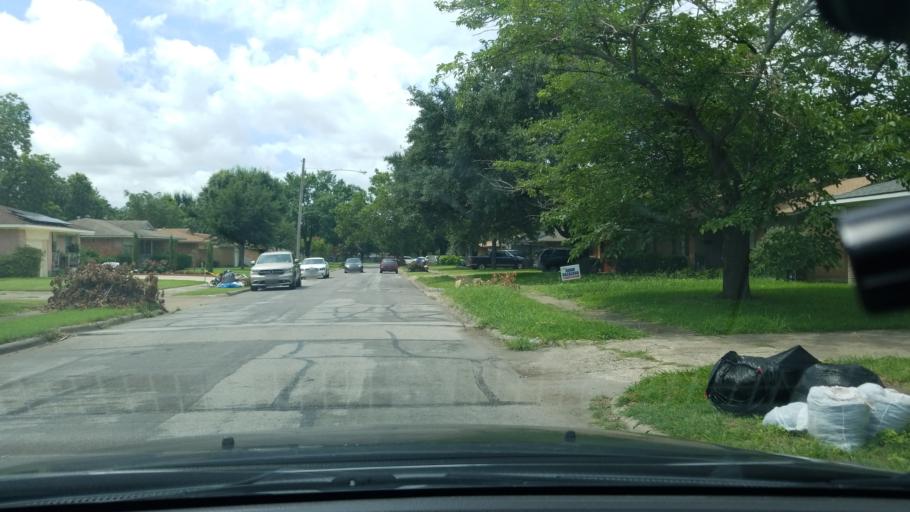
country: US
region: Texas
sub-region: Dallas County
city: Mesquite
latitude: 32.8163
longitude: -96.6777
